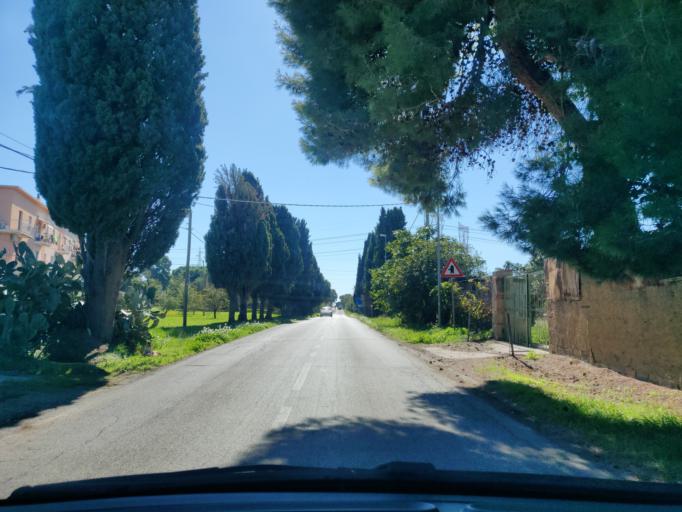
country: IT
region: Latium
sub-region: Citta metropolitana di Roma Capitale
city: Aurelia
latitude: 42.1353
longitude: 11.7883
